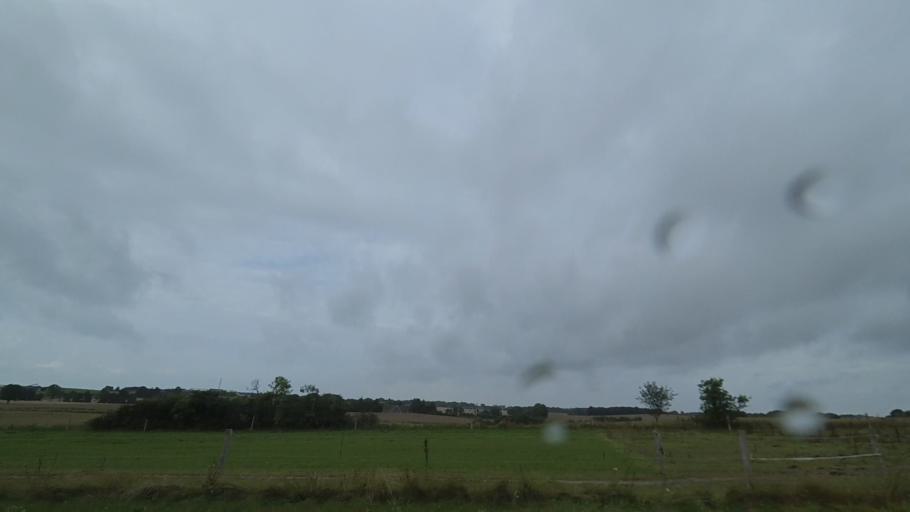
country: DK
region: Central Jutland
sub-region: Syddjurs Kommune
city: Ronde
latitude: 56.3165
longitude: 10.4602
